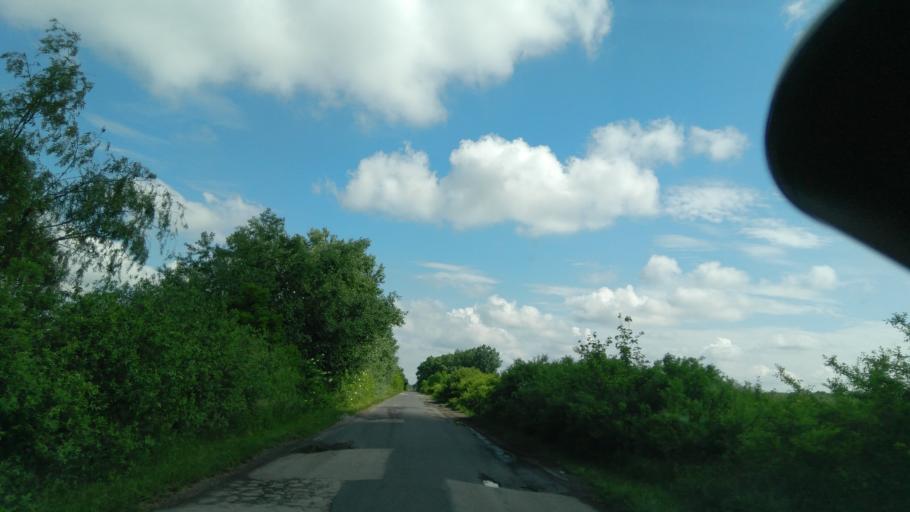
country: HU
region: Bekes
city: Bekes
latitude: 46.8275
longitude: 21.1382
